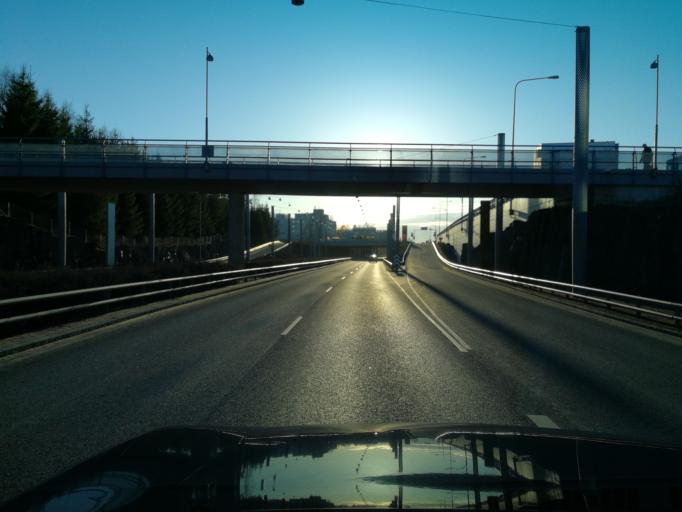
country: FI
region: Uusimaa
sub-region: Helsinki
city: Vantaa
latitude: 60.2047
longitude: 25.1239
